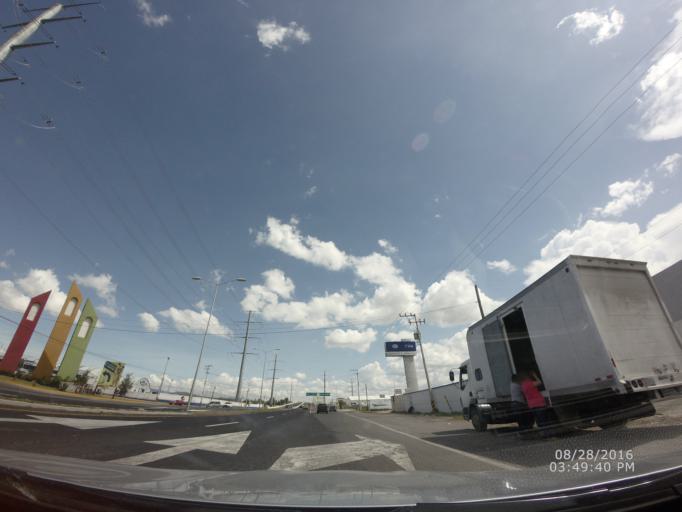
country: MX
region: Hidalgo
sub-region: Mineral de la Reforma
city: Los Tuzos
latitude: 20.0414
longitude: -98.7339
